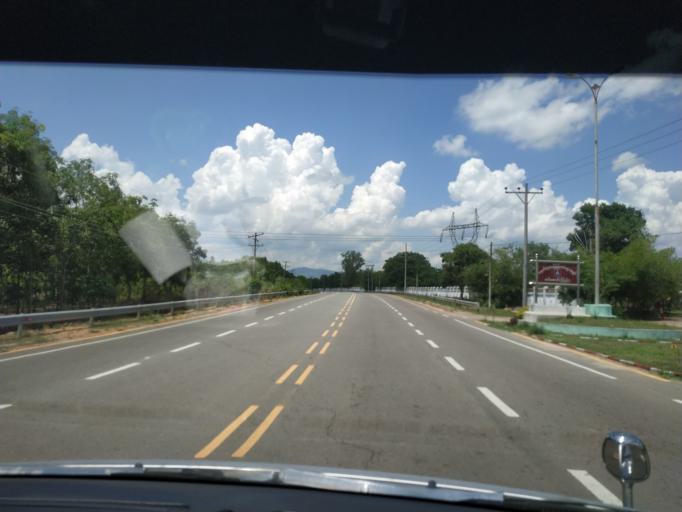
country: MM
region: Mon
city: Kyaikto
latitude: 17.3329
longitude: 97.0362
